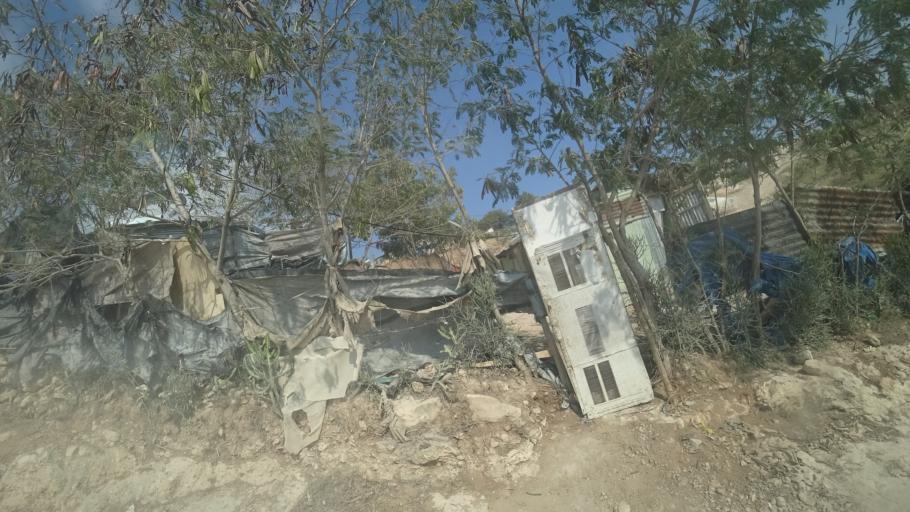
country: HT
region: Ouest
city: Croix des Bouquets
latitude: 18.6607
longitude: -72.2809
